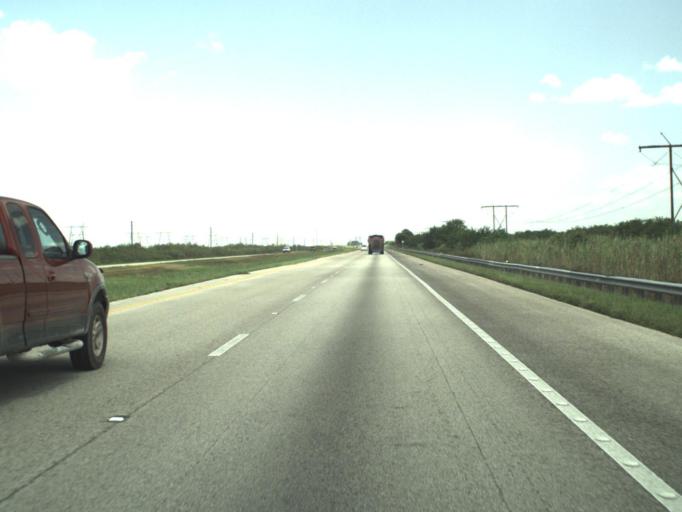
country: US
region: Florida
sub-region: Broward County
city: Weston
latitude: 26.3116
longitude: -80.5196
